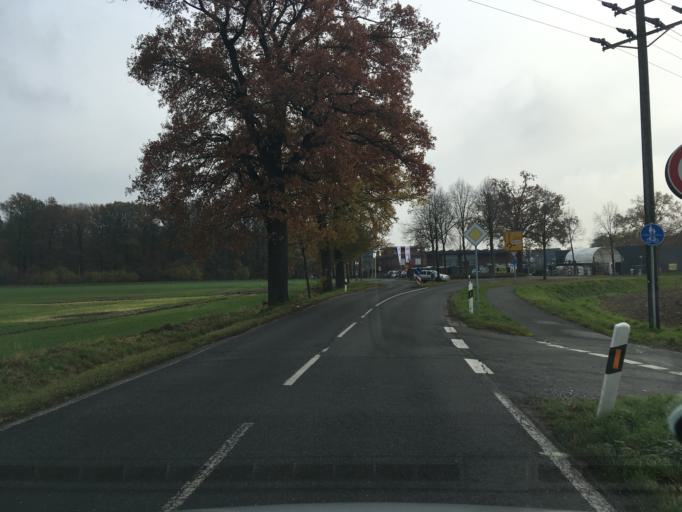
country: DE
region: North Rhine-Westphalia
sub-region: Regierungsbezirk Munster
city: Velen
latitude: 51.9016
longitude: 6.9760
